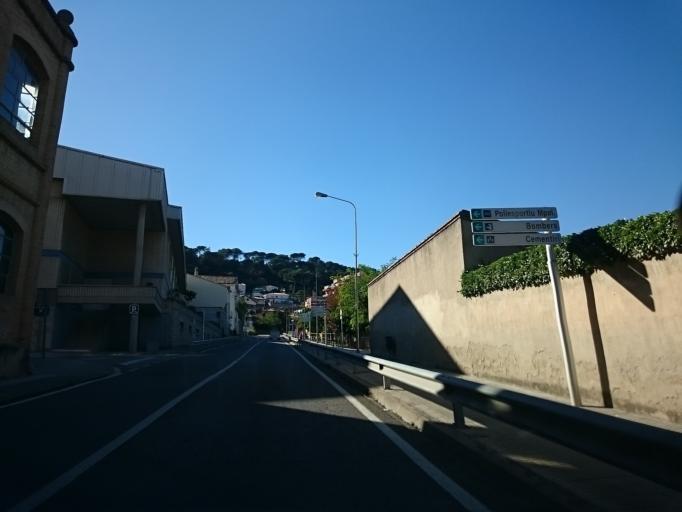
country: ES
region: Catalonia
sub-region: Provincia de Barcelona
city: Capellades
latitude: 41.5273
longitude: 1.6848
